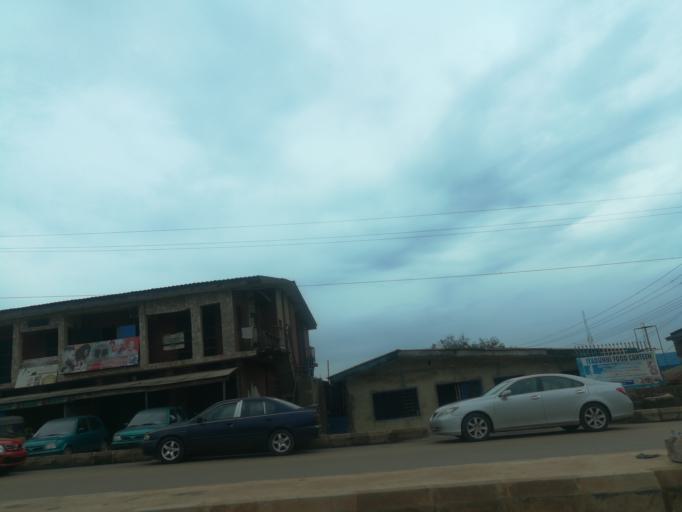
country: NG
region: Oyo
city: Ibadan
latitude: 7.3908
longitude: 3.9381
